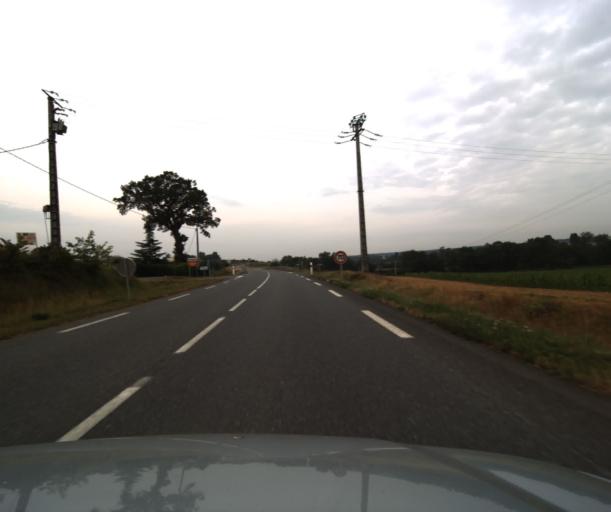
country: FR
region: Midi-Pyrenees
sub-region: Departement du Gers
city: Aubiet
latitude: 43.6589
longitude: 0.7866
